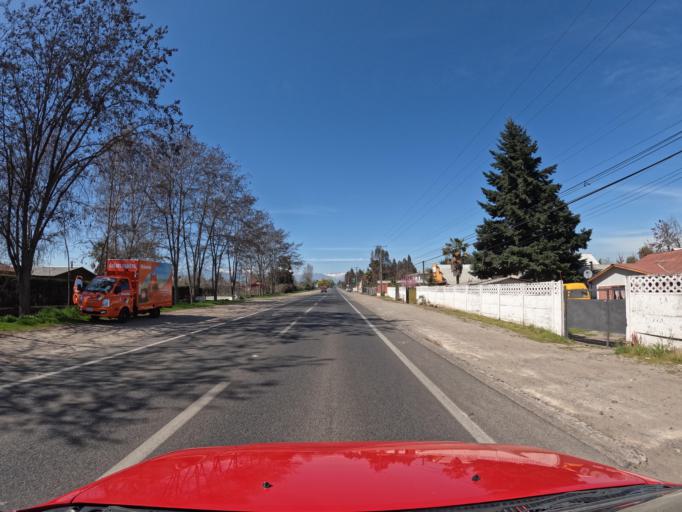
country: CL
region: Maule
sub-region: Provincia de Curico
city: Teno
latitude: -34.9617
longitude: -71.0900
